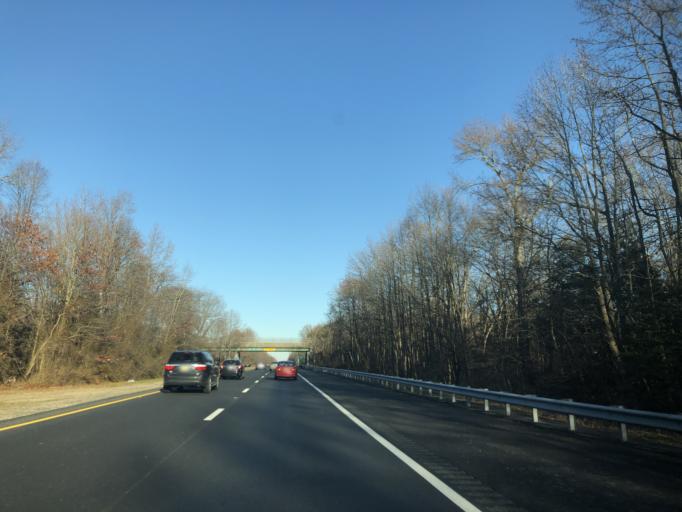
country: US
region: New Jersey
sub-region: Salem County
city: Carneys Point
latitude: 39.7153
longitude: -75.4344
